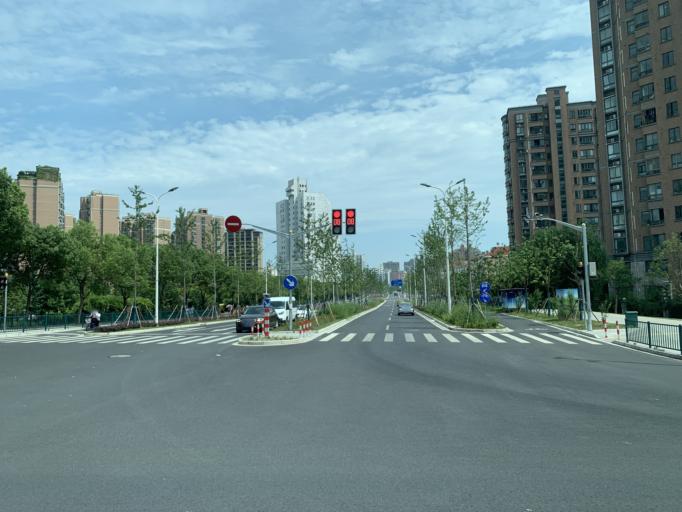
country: CN
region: Shanghai Shi
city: Pudong
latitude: 31.2471
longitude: 121.5447
